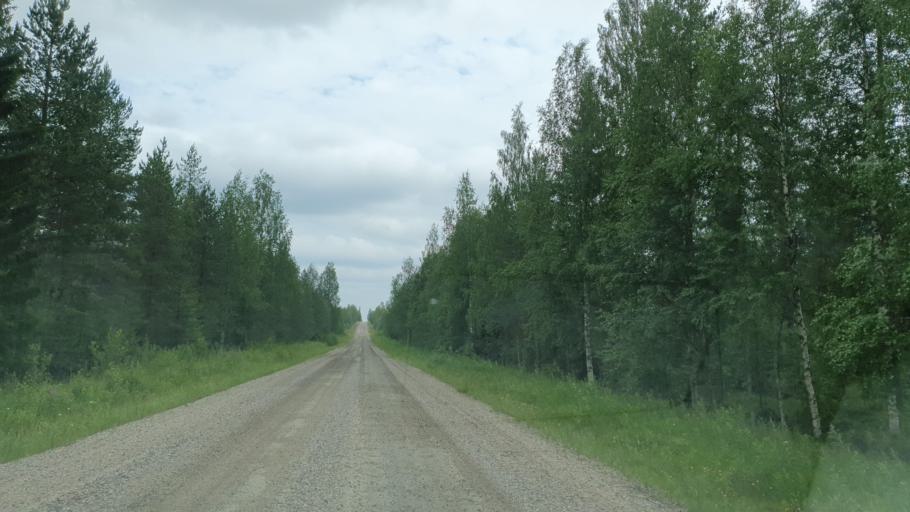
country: FI
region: Kainuu
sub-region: Kehys-Kainuu
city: Kuhmo
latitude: 63.9765
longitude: 29.2806
